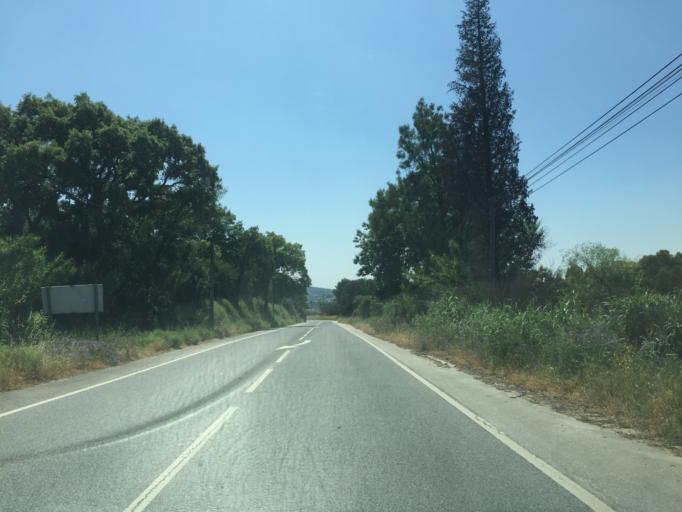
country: PT
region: Santarem
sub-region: Constancia
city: Constancia
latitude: 39.4692
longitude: -8.3335
